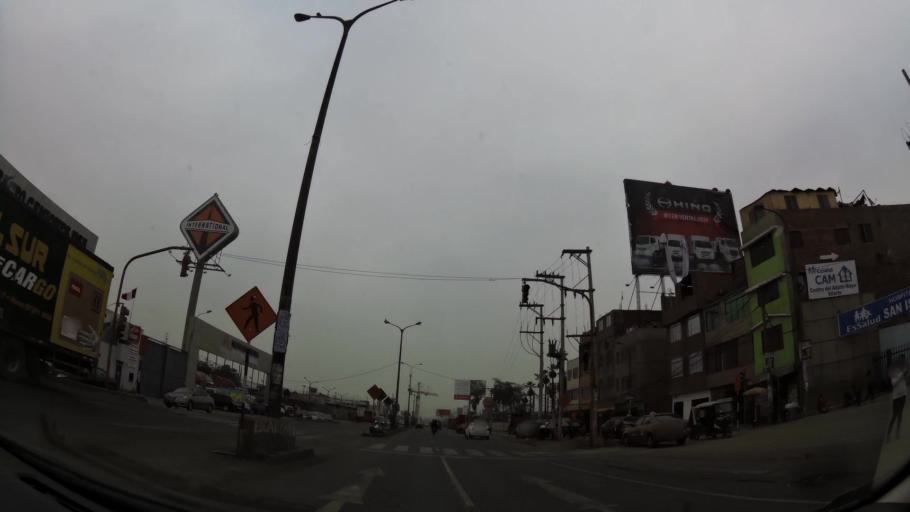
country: PE
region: Lima
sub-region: Lima
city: Vitarte
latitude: -12.0478
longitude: -76.9480
